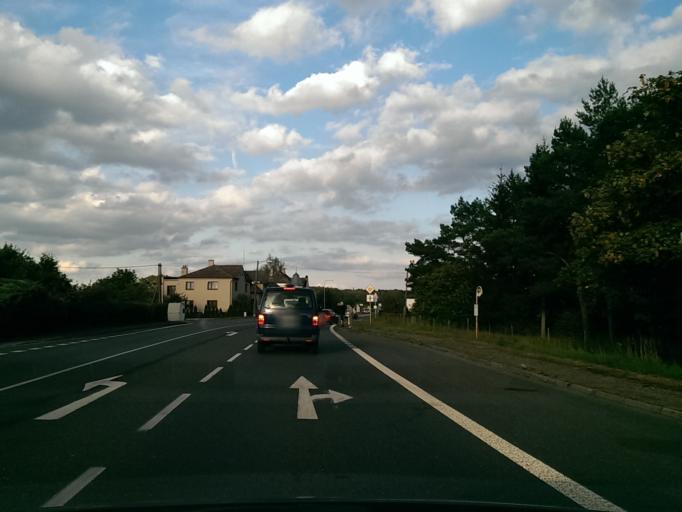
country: CZ
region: Central Bohemia
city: Knezmost
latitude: 50.4450
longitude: 15.0667
